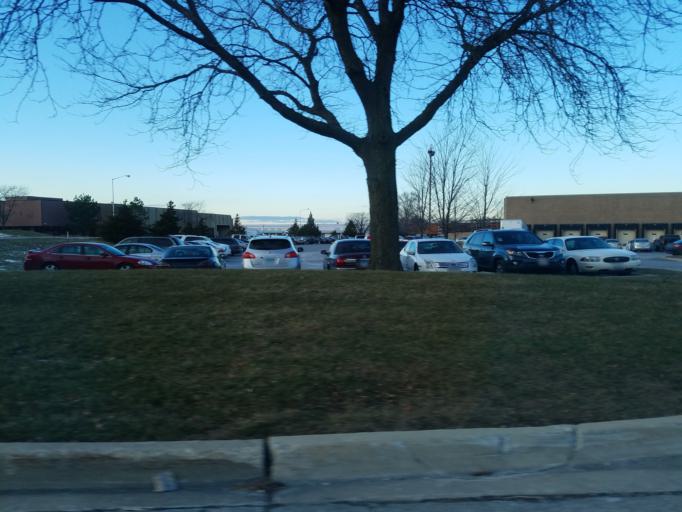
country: US
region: Illinois
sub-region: DuPage County
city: Wood Dale
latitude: 41.9771
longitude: -87.9815
